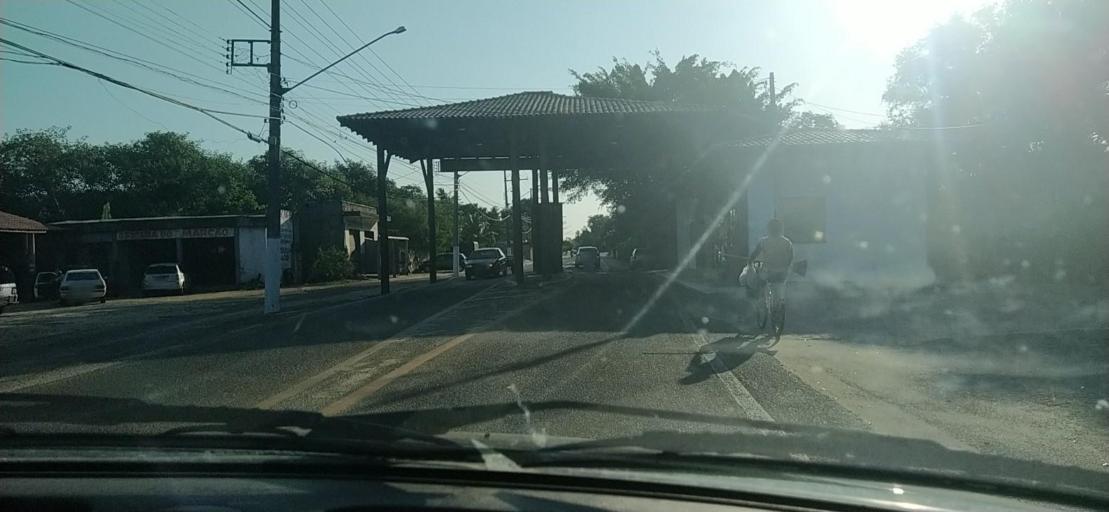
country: BR
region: Espirito Santo
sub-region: Conceicao Da Barra
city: Conceicao da Barra
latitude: -18.5675
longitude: -39.7474
